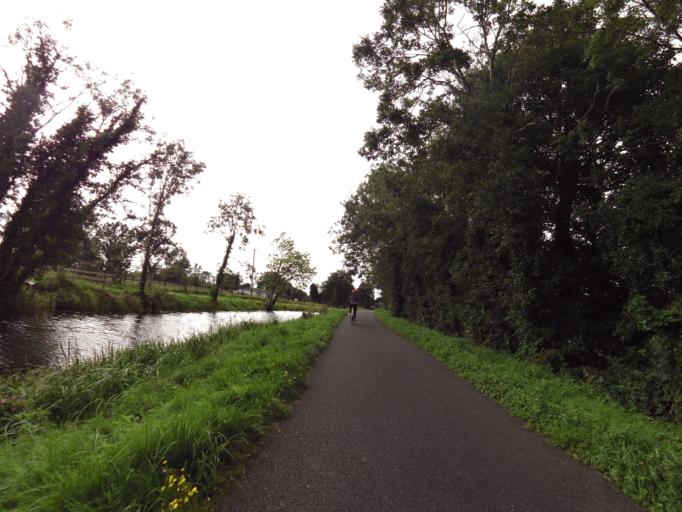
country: IE
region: Leinster
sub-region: An Iarmhi
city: An Muileann gCearr
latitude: 53.5077
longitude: -7.4124
